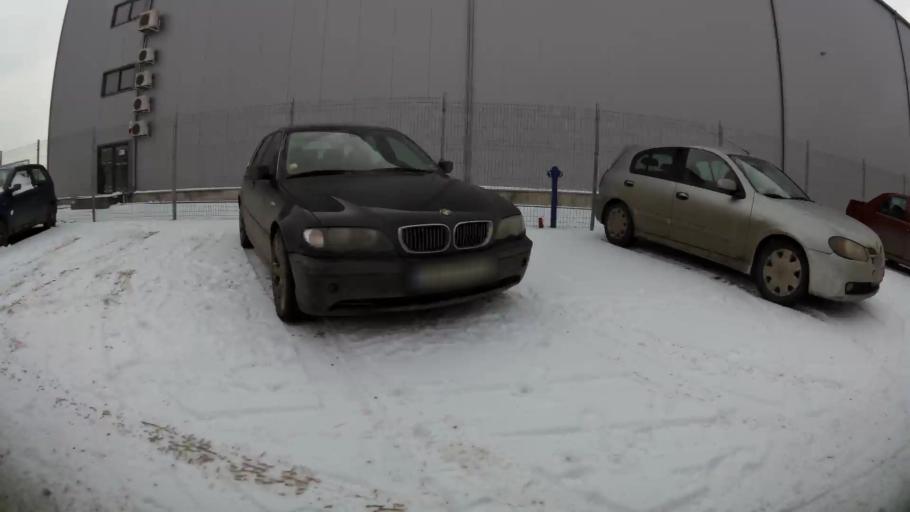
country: BG
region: Sofia-Capital
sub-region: Stolichna Obshtina
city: Sofia
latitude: 42.7054
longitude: 23.4102
